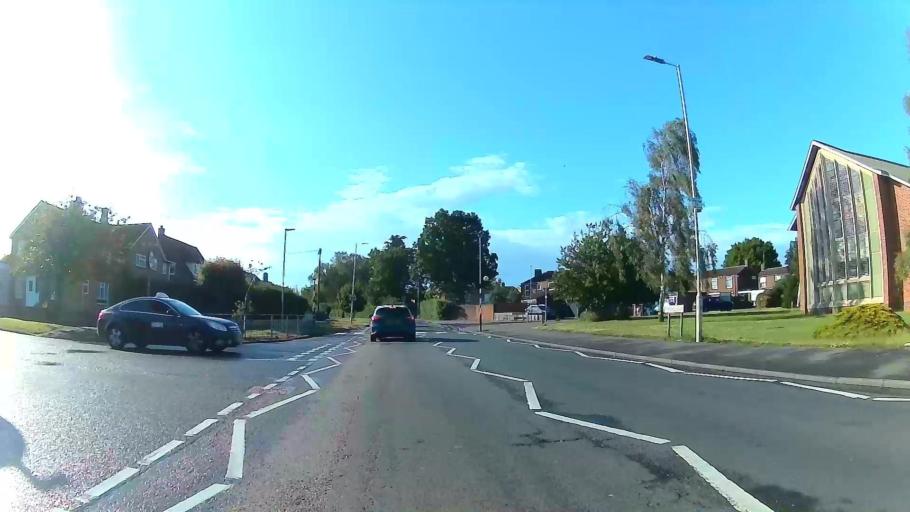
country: GB
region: England
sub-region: Essex
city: Writtle
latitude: 51.7475
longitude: 0.4428
